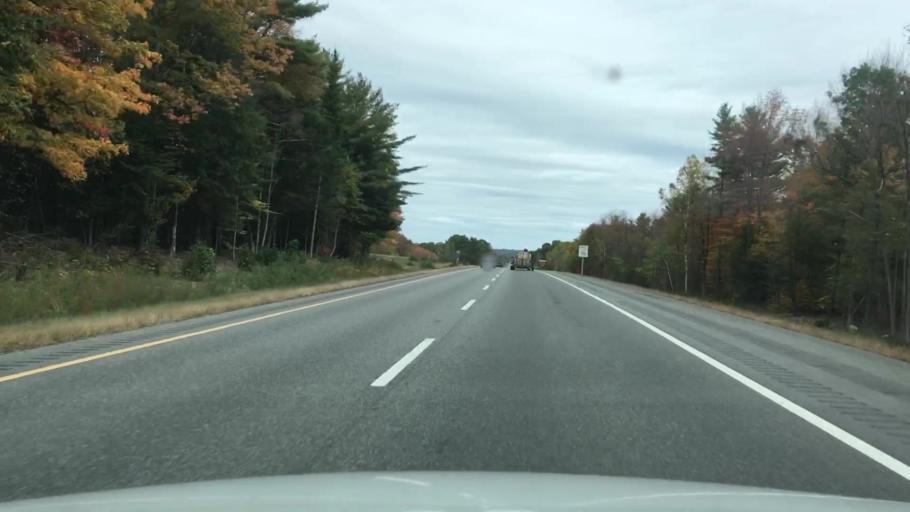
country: US
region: Maine
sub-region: Kennebec County
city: Vassalboro
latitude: 44.4596
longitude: -69.7125
